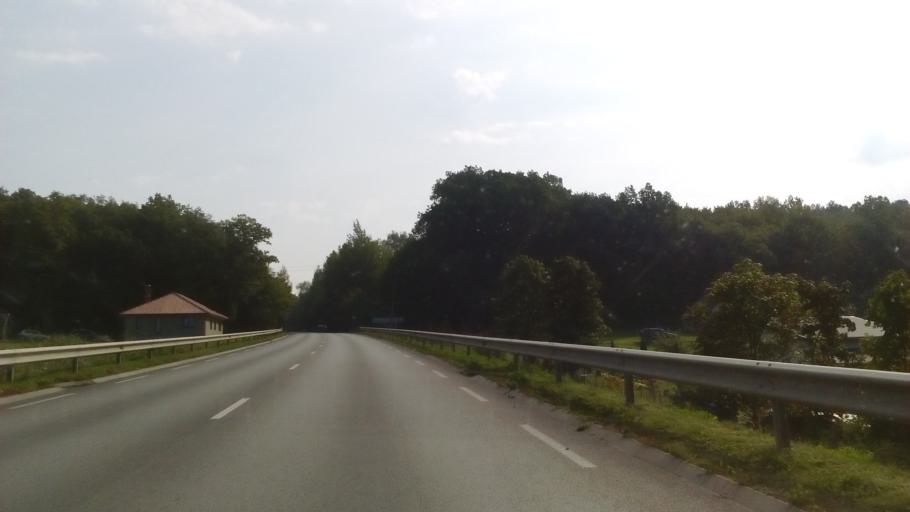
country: LT
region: Alytaus apskritis
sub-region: Alytus
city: Alytus
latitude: 54.3873
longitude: 24.0018
